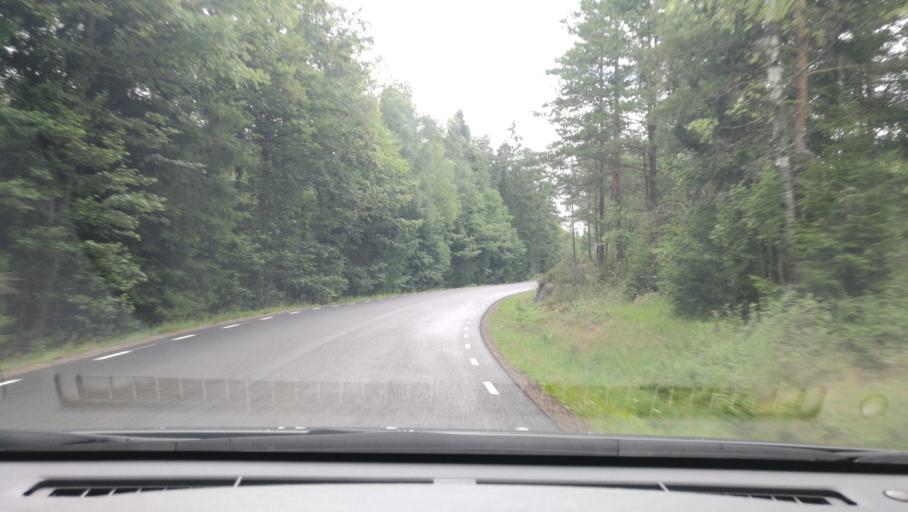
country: SE
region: OEstergoetland
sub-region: Norrkopings Kommun
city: Svartinge
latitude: 58.8159
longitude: 16.0766
